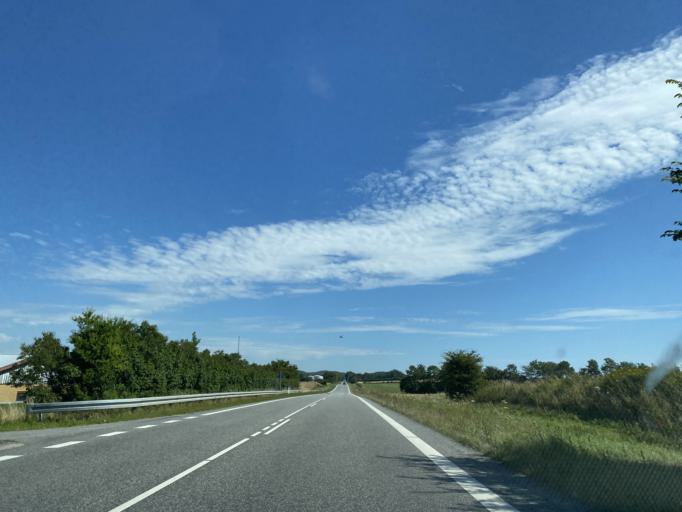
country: DK
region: South Denmark
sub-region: Faaborg-Midtfyn Kommune
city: Faaborg
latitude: 55.1089
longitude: 10.2012
